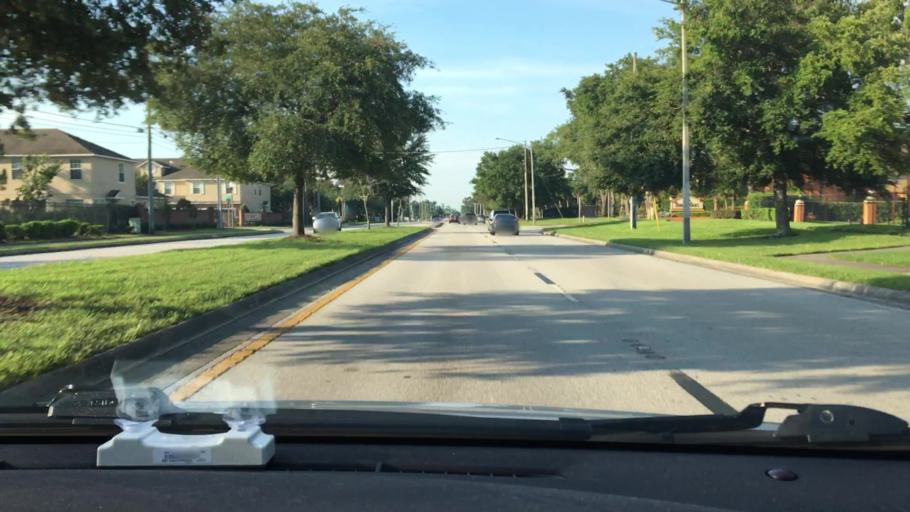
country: US
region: Florida
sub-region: Orange County
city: Union Park
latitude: 28.5877
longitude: -81.2864
